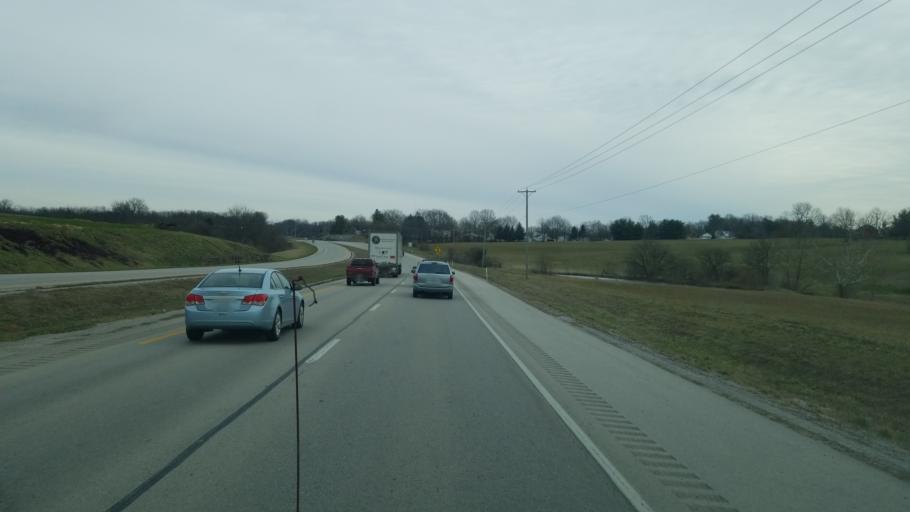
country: US
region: Kentucky
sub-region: Bourbon County
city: Paris
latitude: 38.2253
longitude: -84.2621
